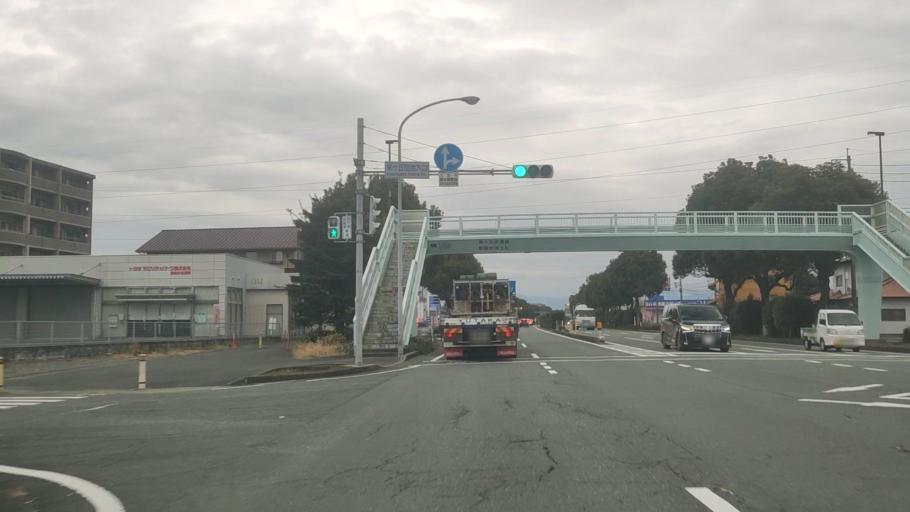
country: JP
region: Kumamoto
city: Ozu
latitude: 32.8567
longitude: 130.7894
